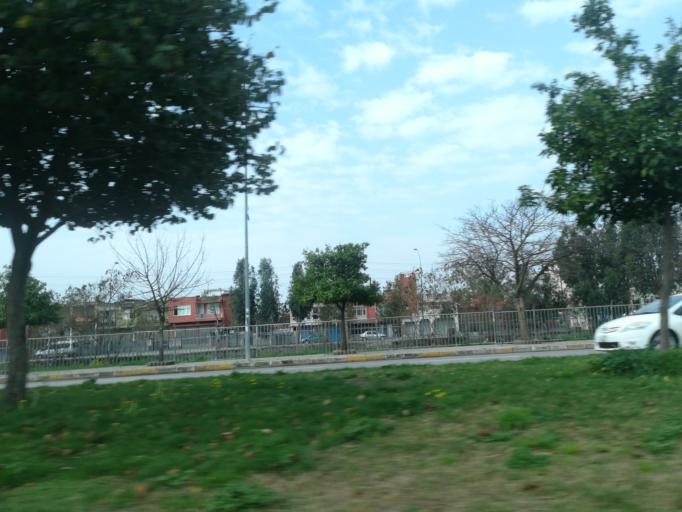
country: TR
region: Adana
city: Yuregir
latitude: 36.9956
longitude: 35.3594
